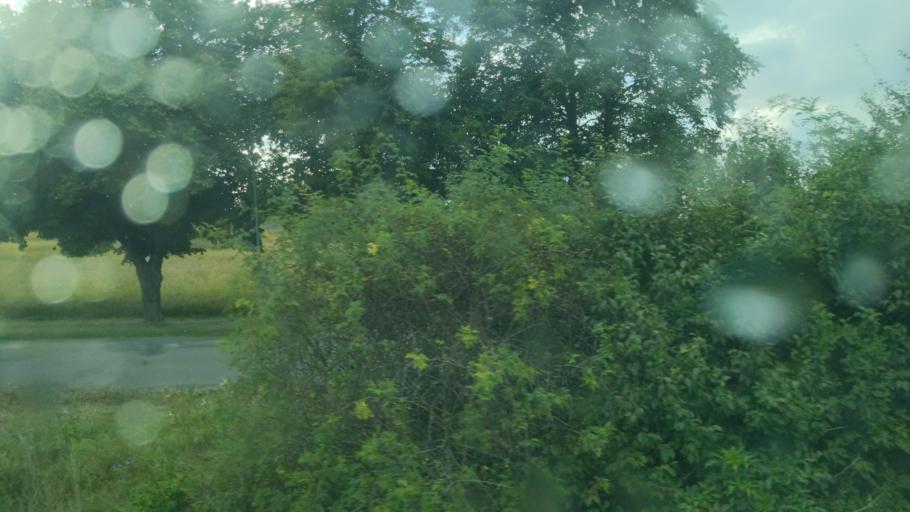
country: CZ
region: Central Bohemia
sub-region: Okres Nymburk
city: Sadska
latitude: 50.1316
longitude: 14.9656
